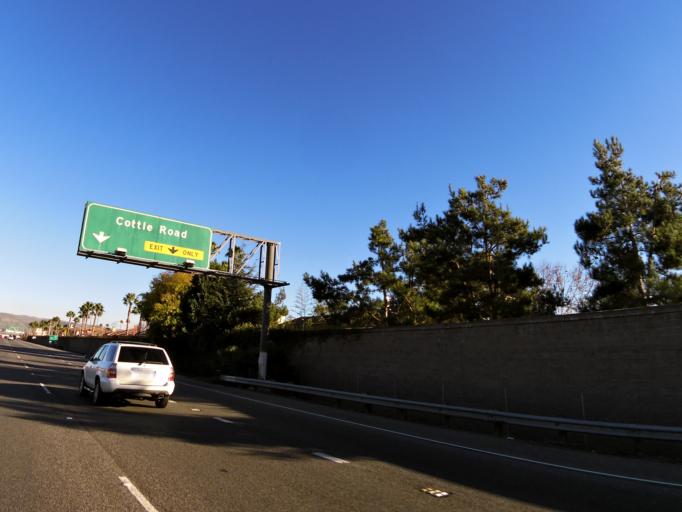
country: US
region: California
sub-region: Santa Clara County
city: Seven Trees
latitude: 37.2431
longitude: -121.8141
